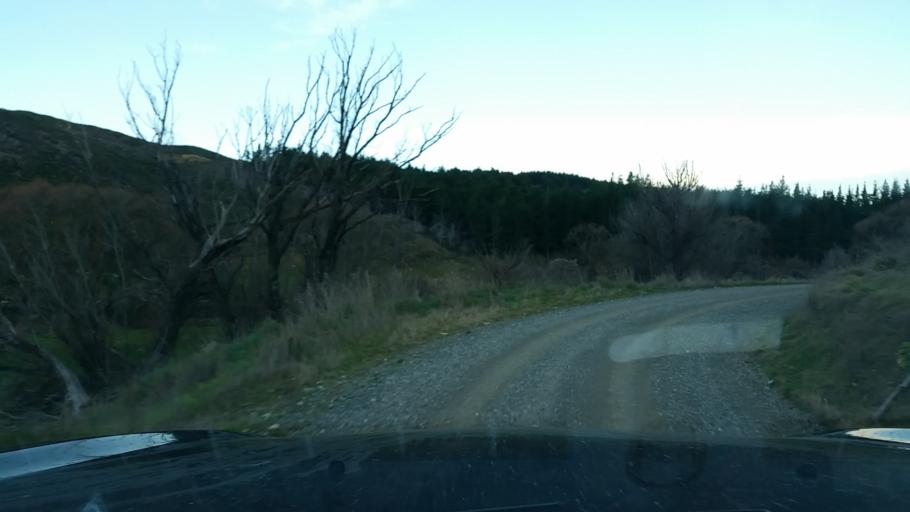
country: NZ
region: Marlborough
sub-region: Marlborough District
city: Blenheim
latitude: -41.5098
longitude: 173.5917
